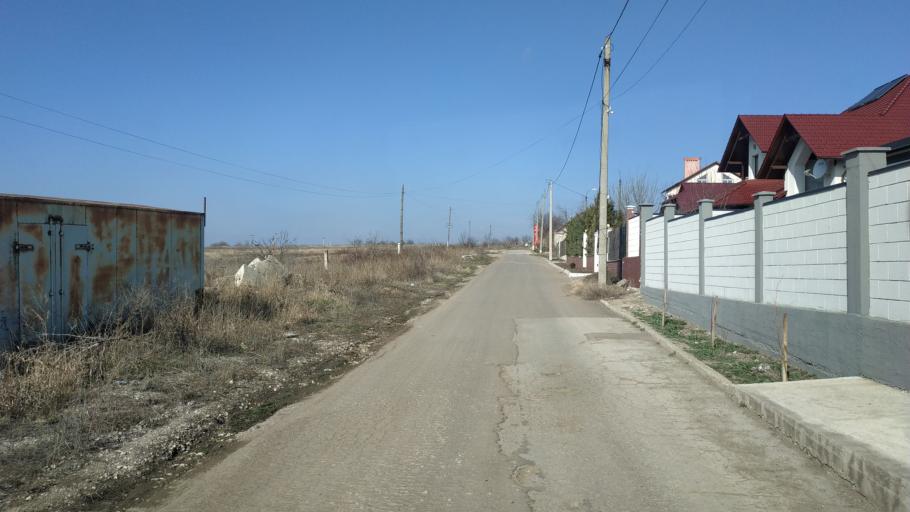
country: MD
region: Chisinau
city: Vatra
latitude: 47.0150
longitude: 28.7409
